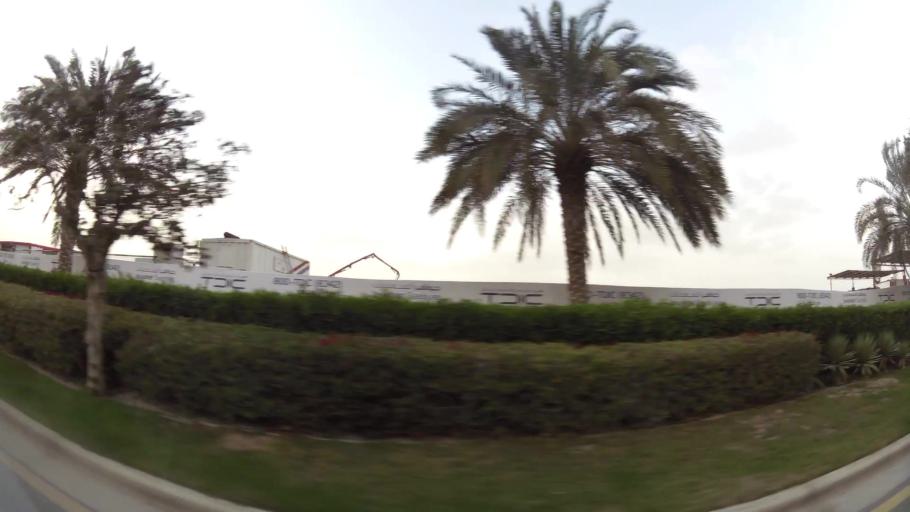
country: AE
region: Abu Dhabi
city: Abu Dhabi
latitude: 24.5333
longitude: 54.4269
